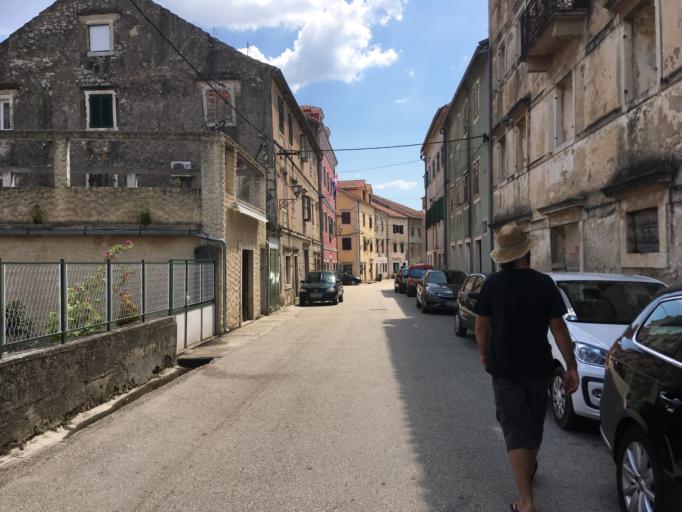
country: HR
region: Sibensko-Kniniska
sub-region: Grad Sibenik
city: Sibenik
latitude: 43.8212
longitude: 15.9222
